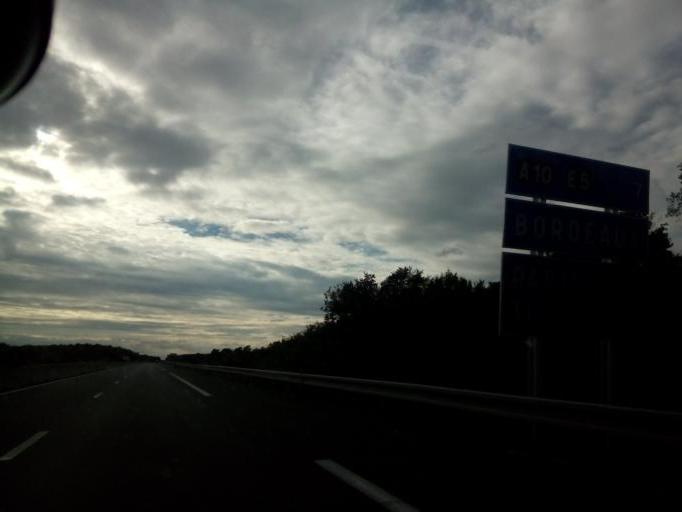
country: FR
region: Centre
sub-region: Departement d'Indre-et-Loire
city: Esvres
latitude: 47.3106
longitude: 0.7887
